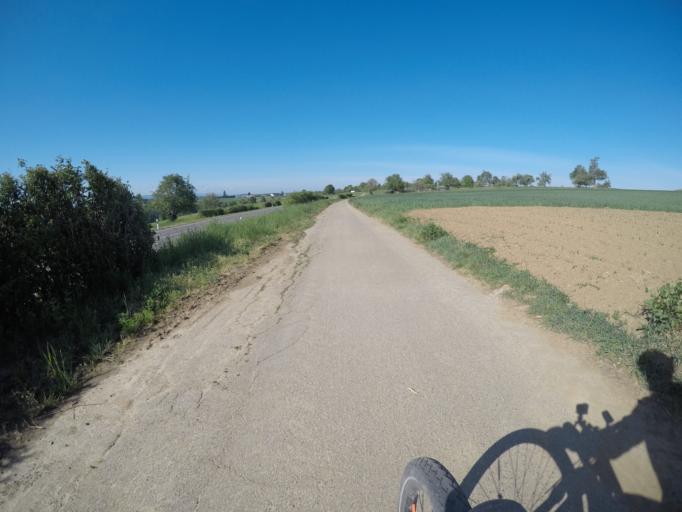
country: DE
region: Baden-Wuerttemberg
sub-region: Regierungsbezirk Stuttgart
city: Schlaitdorf
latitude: 48.6020
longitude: 9.2083
